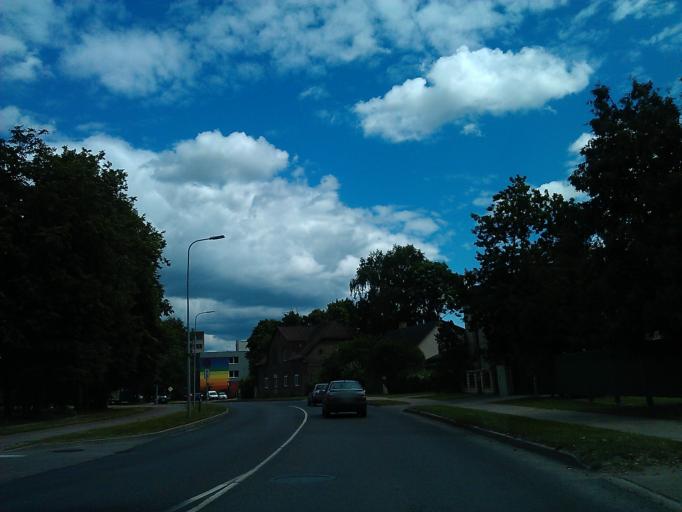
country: LV
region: Jelgava
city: Jelgava
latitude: 56.6366
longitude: 23.7121
